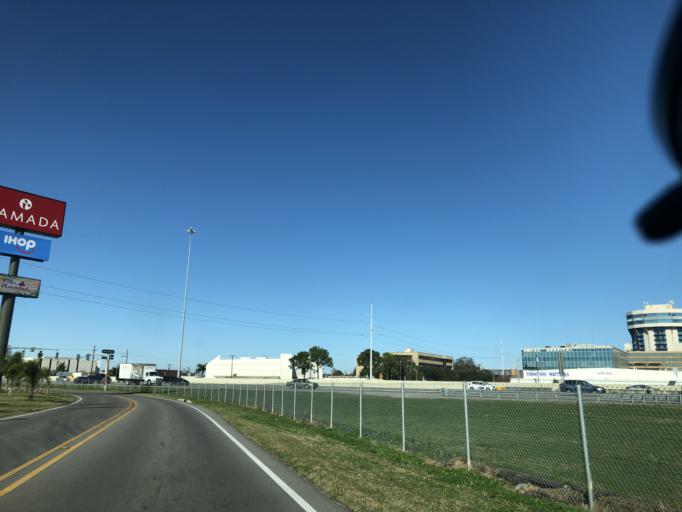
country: US
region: Louisiana
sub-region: Jefferson Parish
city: Metairie
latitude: 29.9967
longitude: -90.1587
